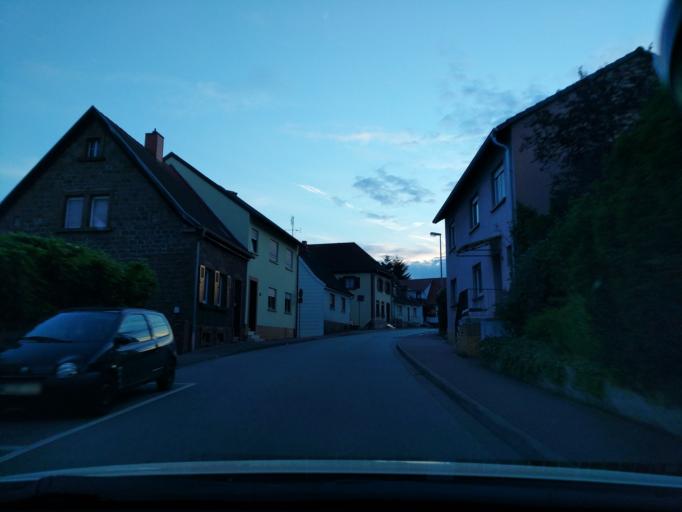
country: DE
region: Rheinland-Pfalz
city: Weilerbach
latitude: 49.4822
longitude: 7.6285
